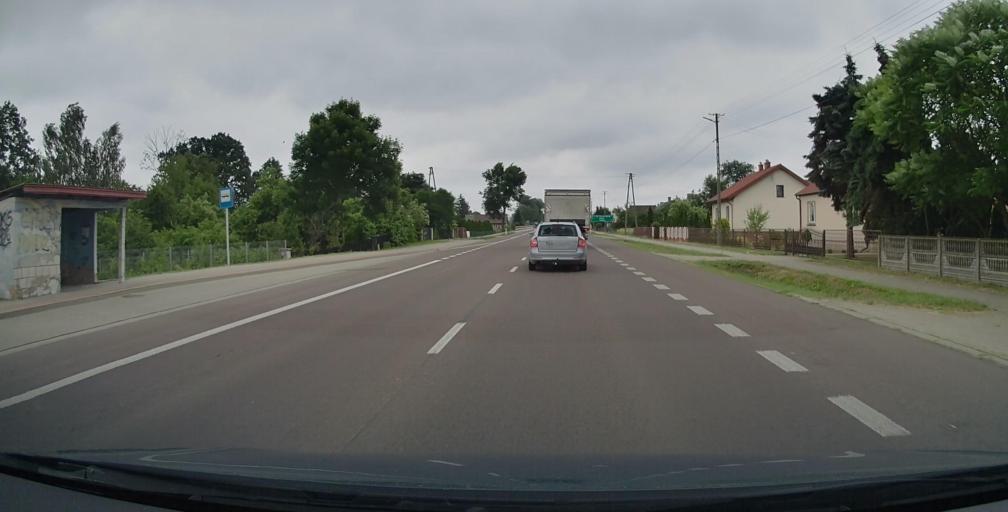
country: PL
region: Lublin Voivodeship
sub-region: Powiat bialski
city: Rzeczyca
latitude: 52.0206
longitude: 22.7232
